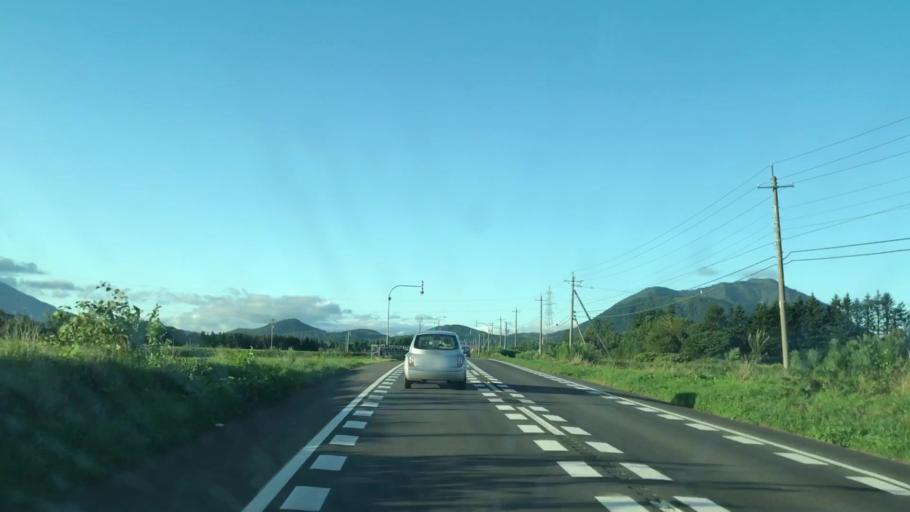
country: JP
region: Hokkaido
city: Niseko Town
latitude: 42.7171
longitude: 140.8593
